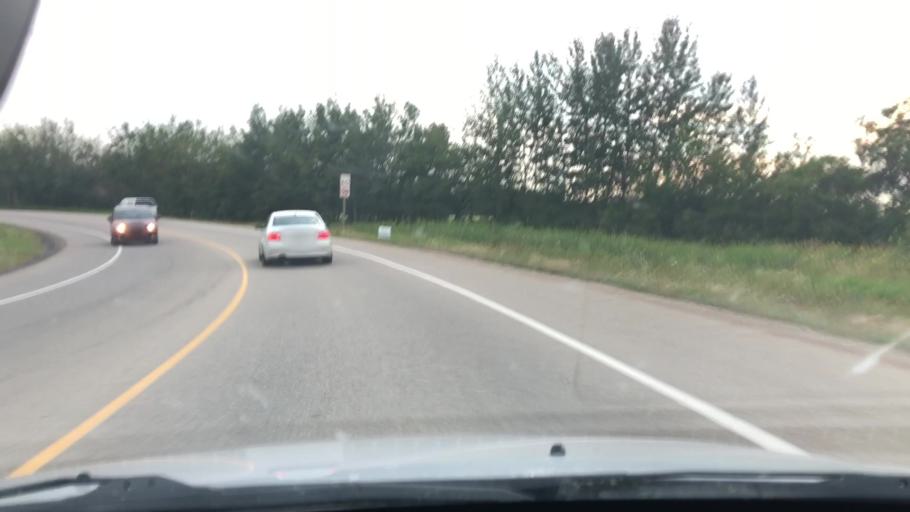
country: CA
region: Alberta
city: Devon
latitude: 53.4591
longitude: -113.6392
